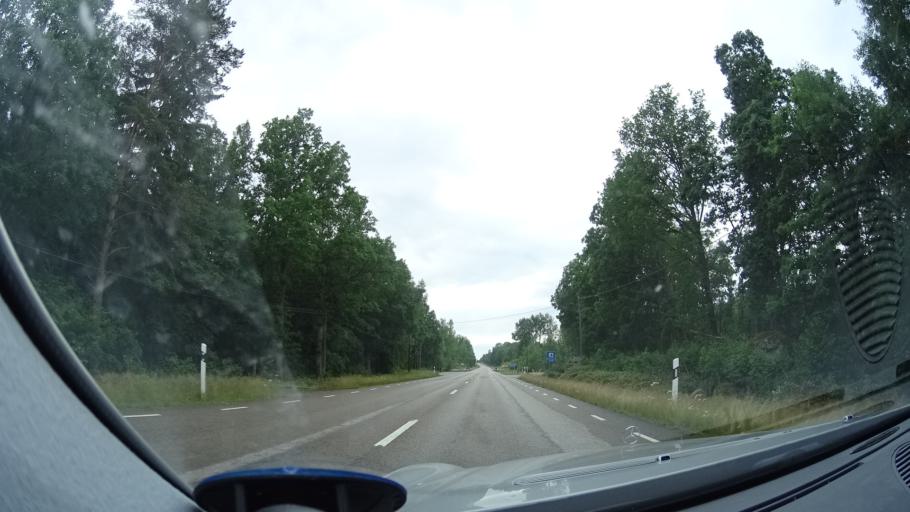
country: SE
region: Kronoberg
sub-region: Tingsryds Kommun
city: Tingsryd
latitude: 56.4426
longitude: 14.9803
